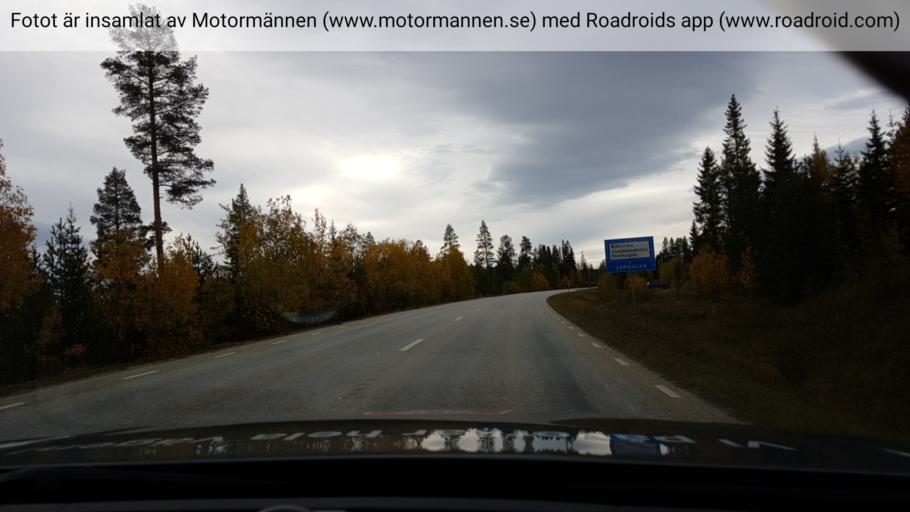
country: SE
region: Jaemtland
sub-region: Bergs Kommun
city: Hoverberg
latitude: 62.4839
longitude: 14.2305
